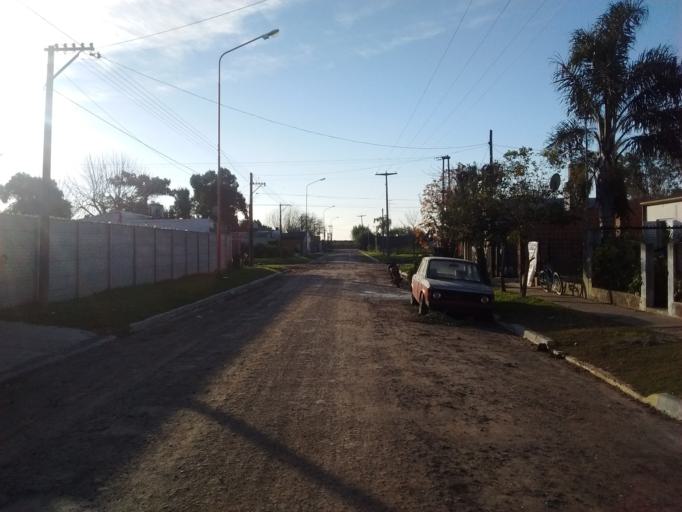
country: AR
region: Santa Fe
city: Galvez
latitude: -32.1653
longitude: -61.1591
